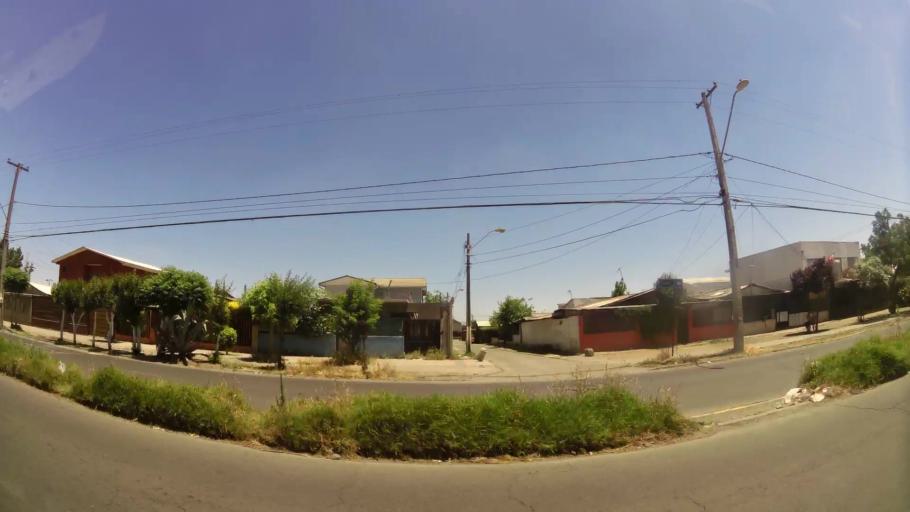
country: CL
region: Santiago Metropolitan
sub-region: Provincia de Santiago
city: La Pintana
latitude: -33.5574
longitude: -70.6555
